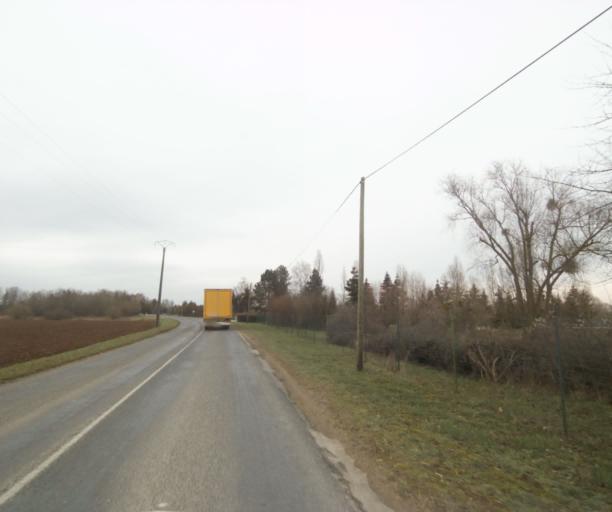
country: FR
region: Champagne-Ardenne
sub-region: Departement de la Haute-Marne
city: Villiers-en-Lieu
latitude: 48.6477
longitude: 4.9063
